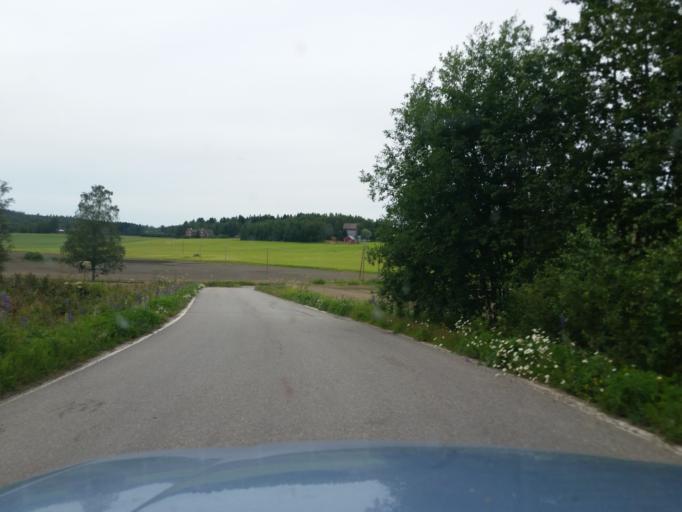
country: FI
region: Uusimaa
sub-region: Helsinki
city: Sammatti
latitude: 60.4735
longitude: 23.8231
